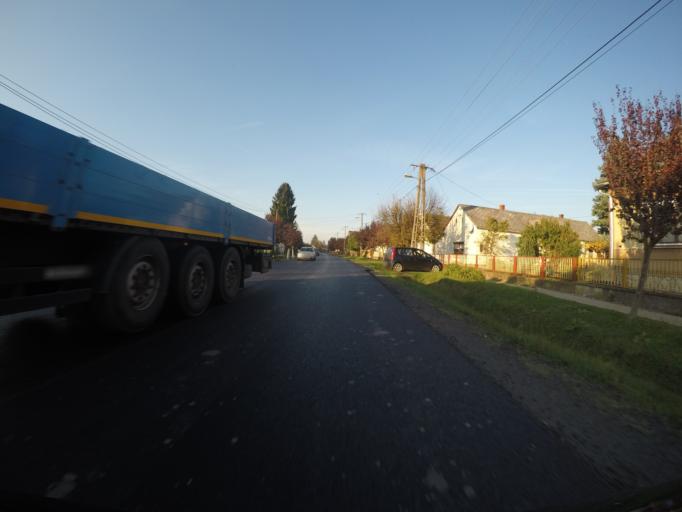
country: HU
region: Somogy
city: Barcs
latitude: 45.9838
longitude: 17.5903
